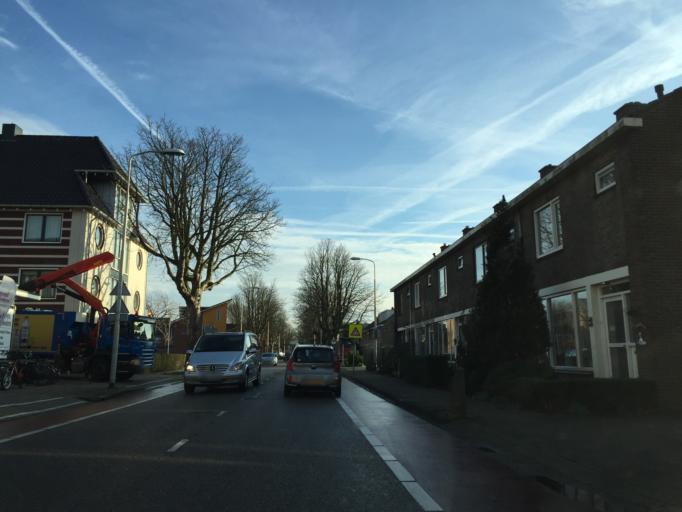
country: NL
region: South Holland
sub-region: Gemeente Zoetermeer
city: Zoetermeer
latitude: 52.0504
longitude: 4.5003
